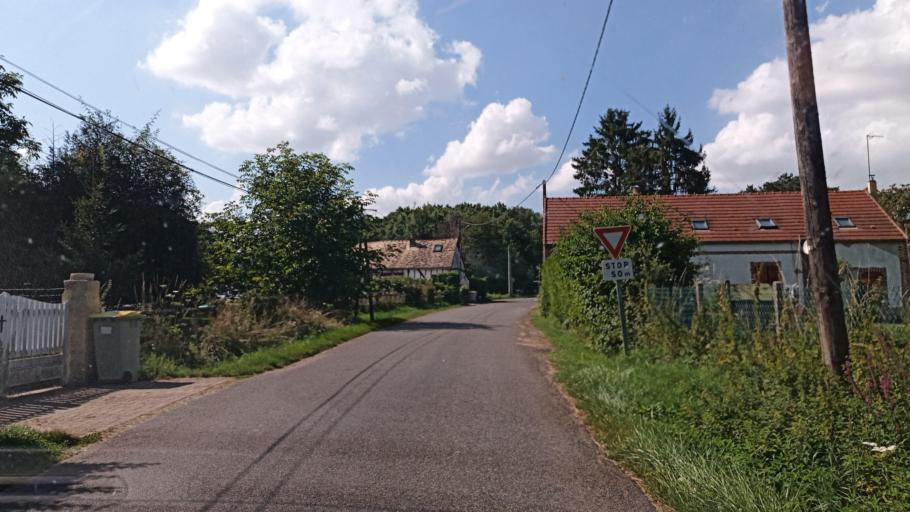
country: FR
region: Bourgogne
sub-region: Departement de l'Yonne
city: Saint-Valerien
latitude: 48.1359
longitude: 3.0931
